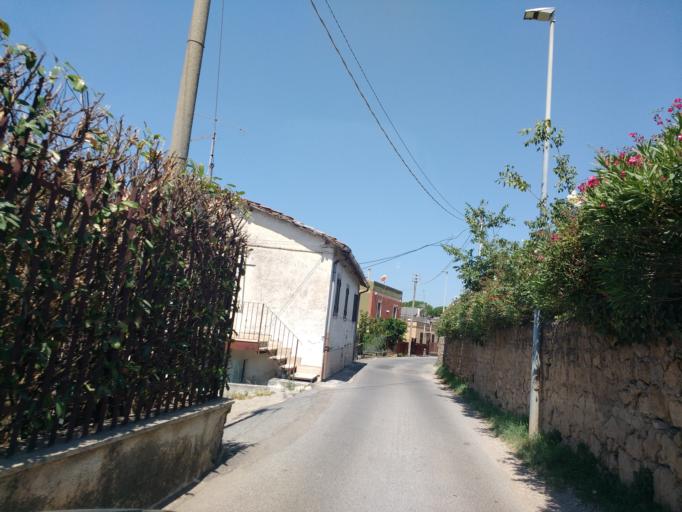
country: IT
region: Latium
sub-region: Citta metropolitana di Roma Capitale
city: Villa Adriana
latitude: 41.9491
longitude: 12.7799
